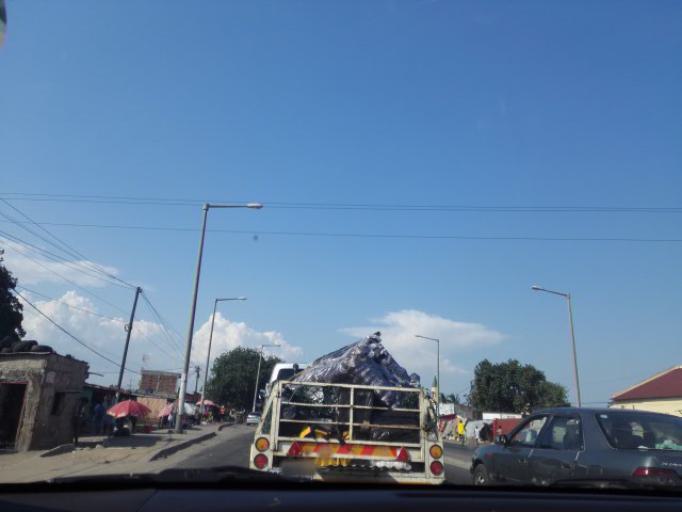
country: MZ
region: Maputo City
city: Maputo
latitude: -25.8850
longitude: 32.5663
